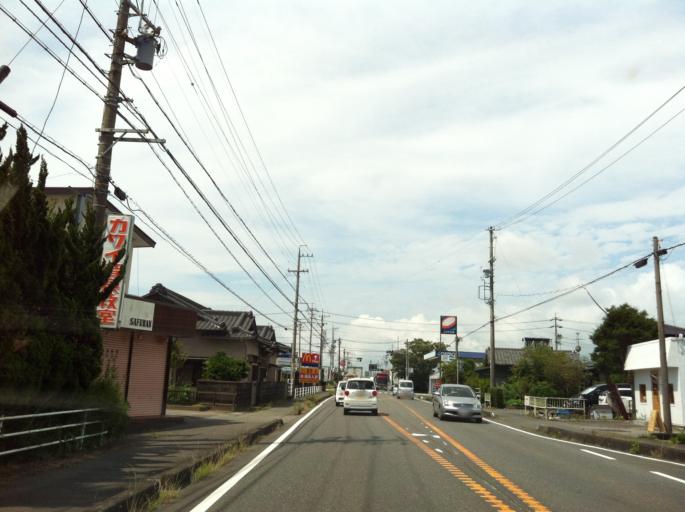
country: JP
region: Shizuoka
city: Fujieda
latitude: 34.8169
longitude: 138.2801
